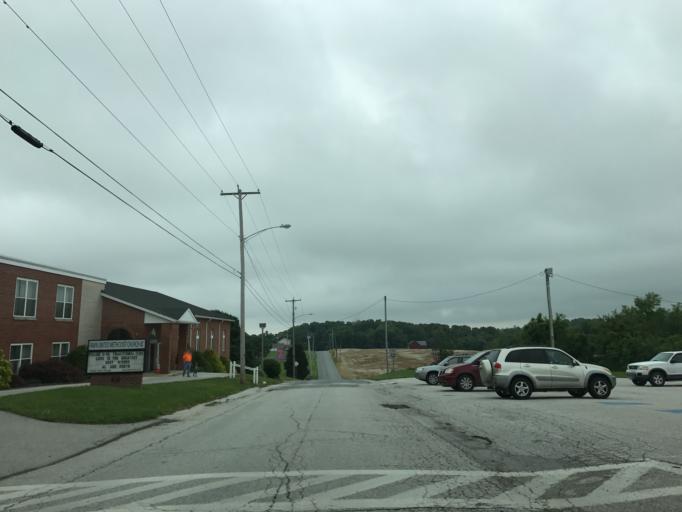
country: US
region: Pennsylvania
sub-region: York County
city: Susquehanna Trails
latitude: 39.7261
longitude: -76.4519
